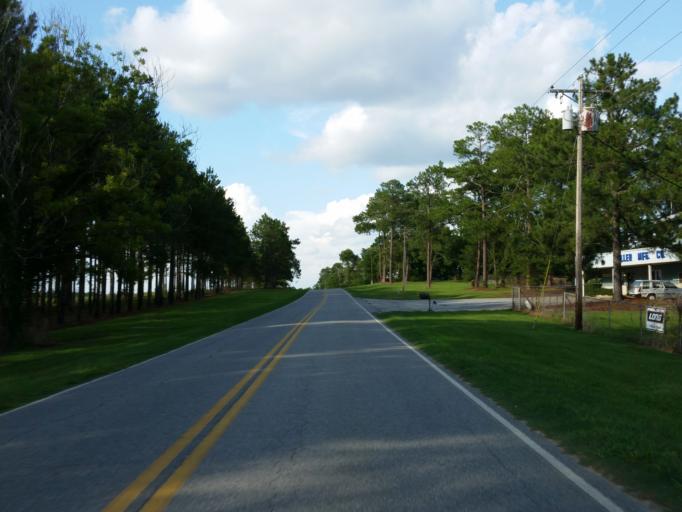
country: US
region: Georgia
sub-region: Crisp County
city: Cordele
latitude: 31.9951
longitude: -83.8653
